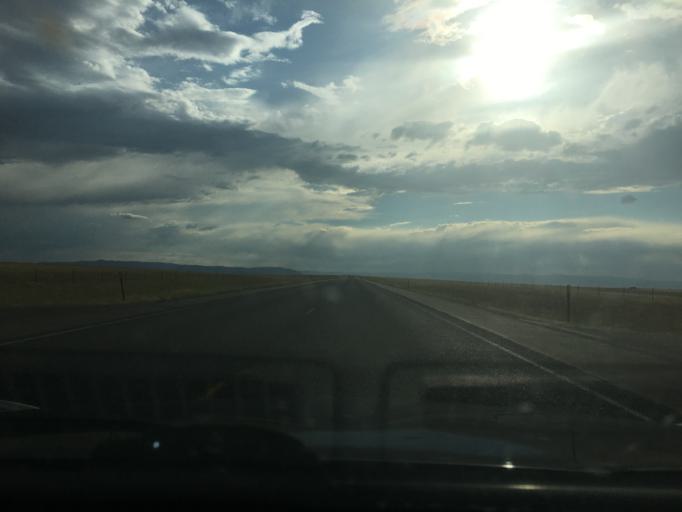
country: US
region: Wyoming
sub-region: Albany County
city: Laramie
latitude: 41.3289
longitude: -105.6918
